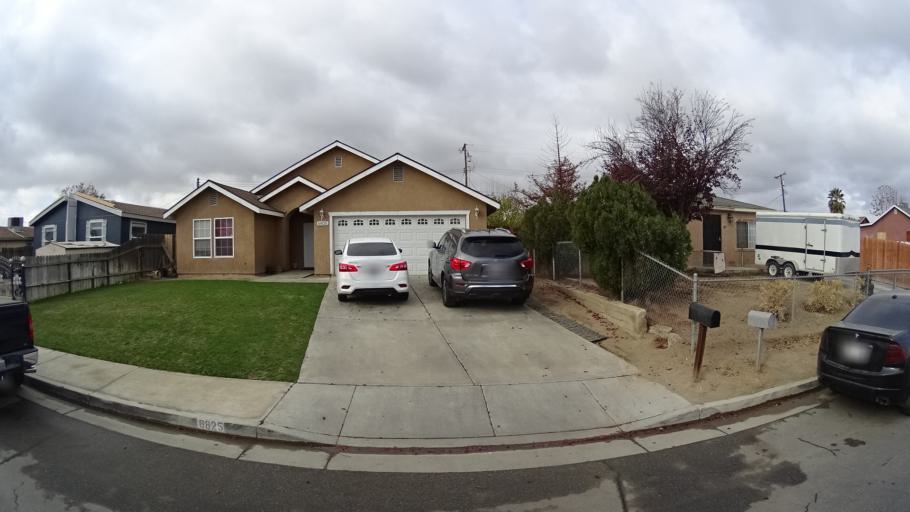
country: US
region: California
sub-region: Kern County
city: Greenfield
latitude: 35.2927
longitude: -119.0086
